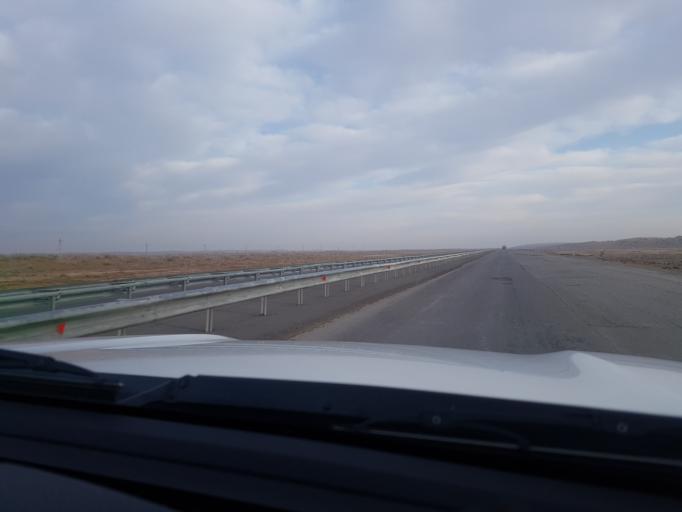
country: TM
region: Ahal
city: Abadan
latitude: 38.5593
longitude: 58.5084
